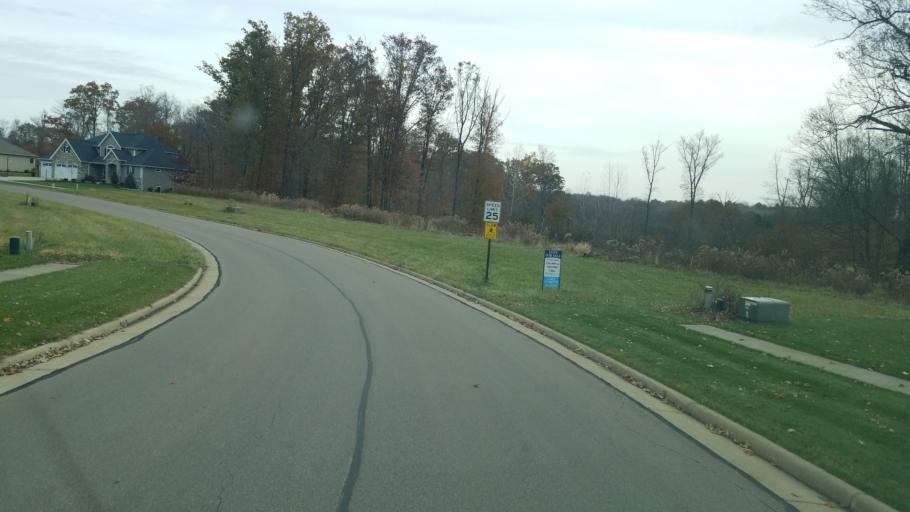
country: US
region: Ohio
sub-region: Richland County
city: Ontario
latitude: 40.7546
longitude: -82.6392
